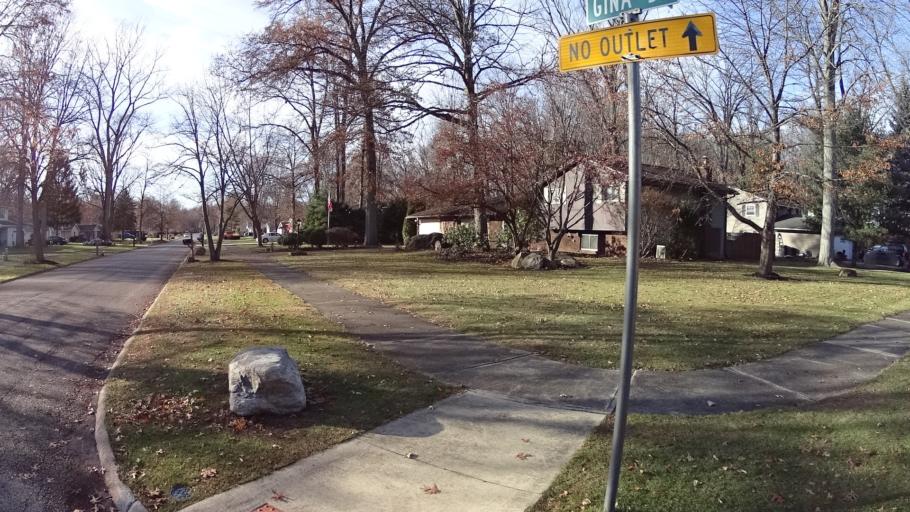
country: US
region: Ohio
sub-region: Lorain County
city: North Ridgeville
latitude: 41.3937
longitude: -81.9939
